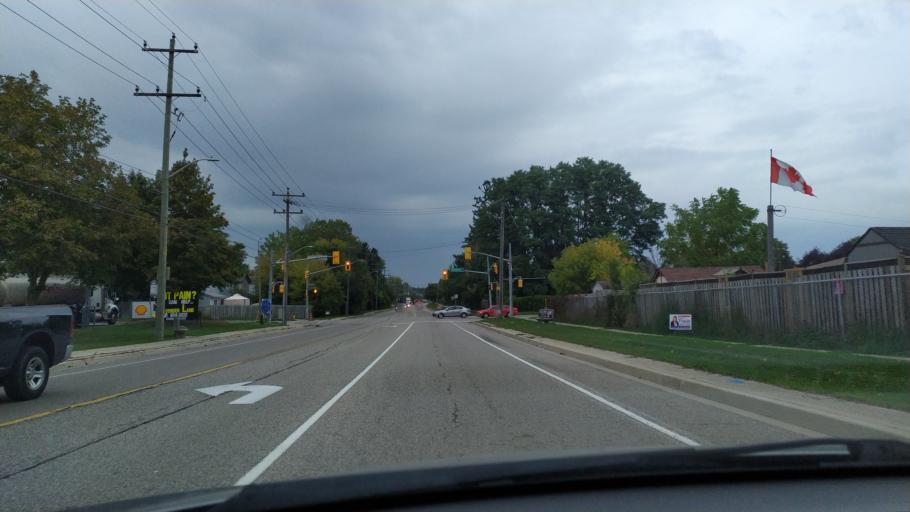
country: CA
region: Ontario
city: Waterloo
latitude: 43.4958
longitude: -80.5009
